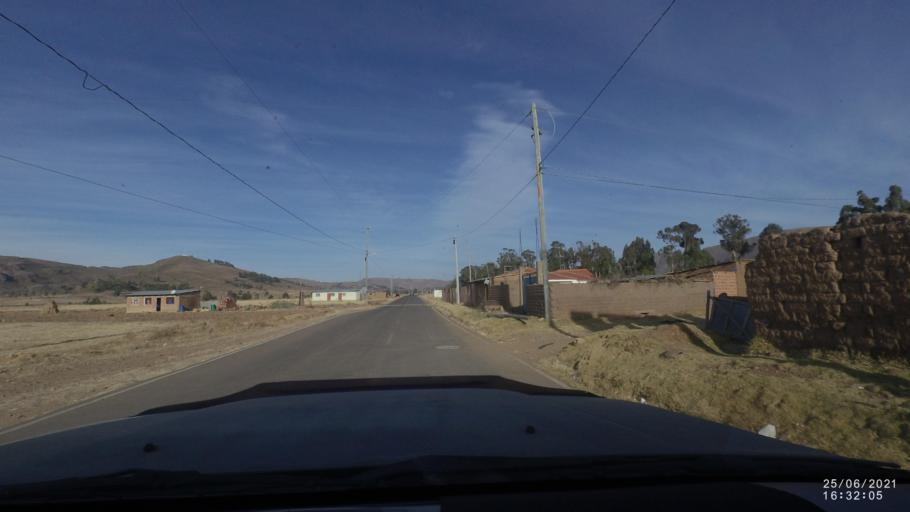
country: BO
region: Cochabamba
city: Arani
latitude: -17.8045
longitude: -65.7986
